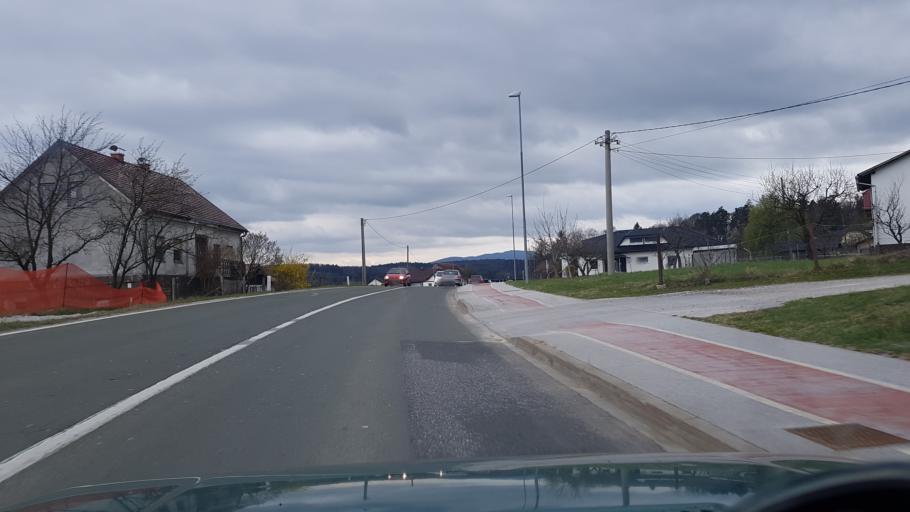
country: SI
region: Slovenska Bistrica
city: Slovenska Bistrica
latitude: 46.3798
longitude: 15.5602
